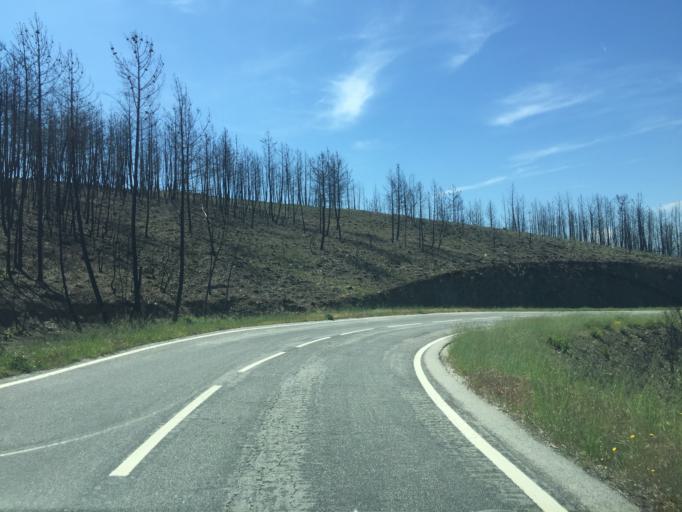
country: PT
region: Coimbra
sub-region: Pampilhosa da Serra
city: Pampilhosa da Serra
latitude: 40.0095
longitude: -7.9726
